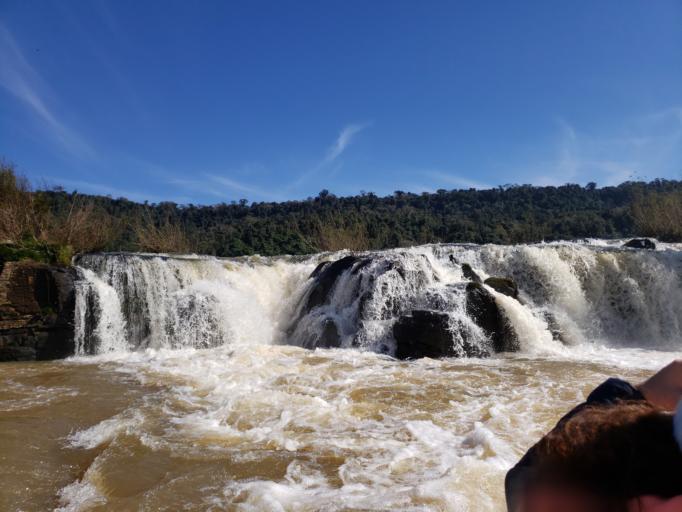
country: BR
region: Rio Grande do Sul
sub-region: Tres Passos
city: Tres Passos
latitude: -27.1490
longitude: -53.8873
